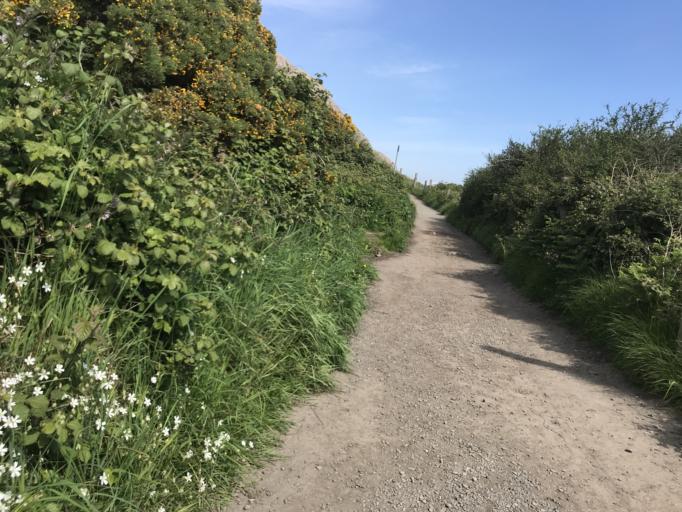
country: IE
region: Leinster
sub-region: Wicklow
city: Bray
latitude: 53.1757
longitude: -6.0749
